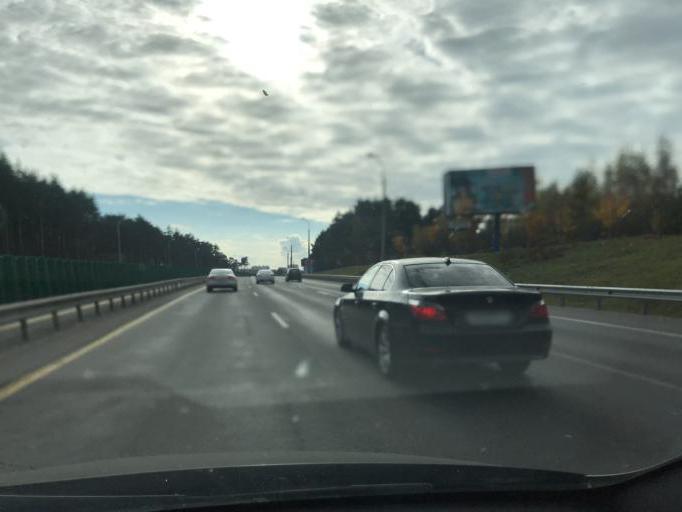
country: BY
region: Minsk
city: Vyaliki Trastsyanets
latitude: 53.8783
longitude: 27.6962
